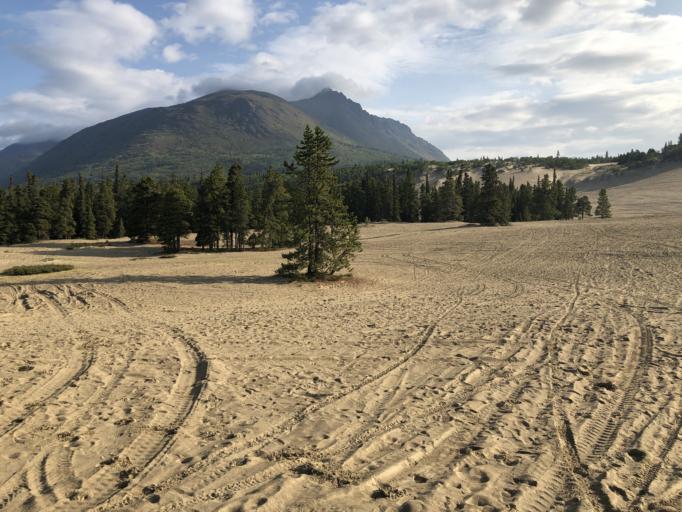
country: CA
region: Yukon
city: Whitehorse
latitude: 60.1855
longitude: -134.6980
